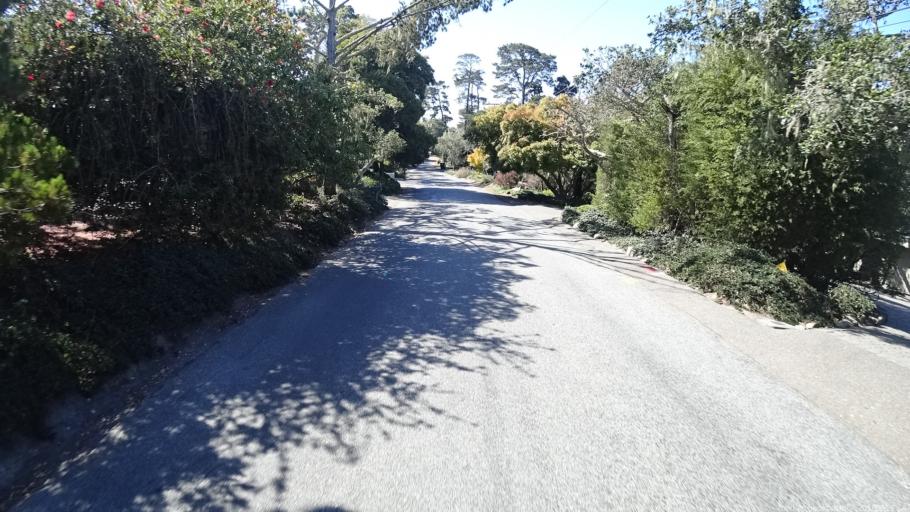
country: US
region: California
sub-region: Monterey County
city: Carmel-by-the-Sea
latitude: 36.5517
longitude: -121.9141
